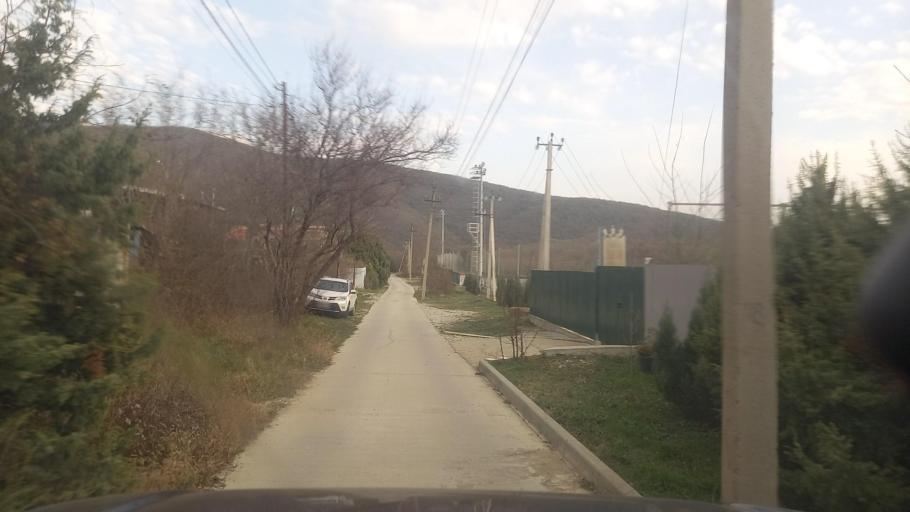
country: RU
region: Krasnodarskiy
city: Myskhako
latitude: 44.6664
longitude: 37.6783
